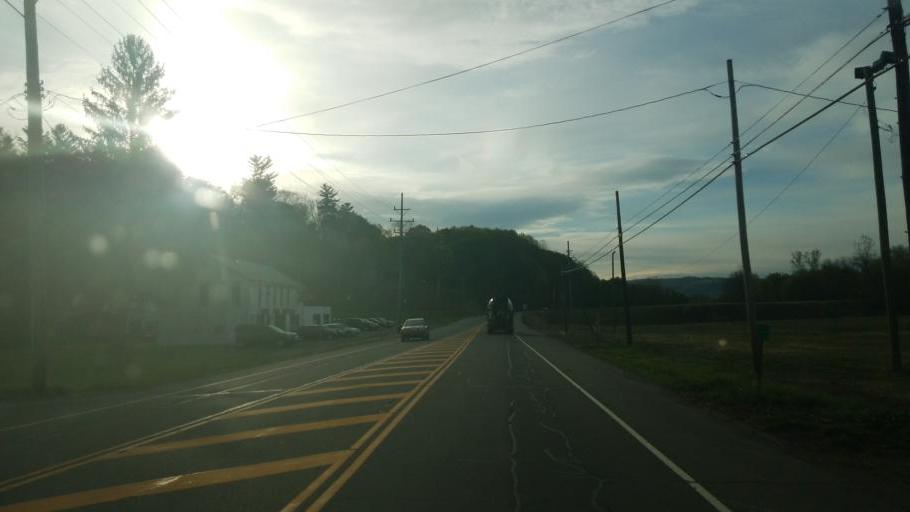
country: US
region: New York
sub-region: Steuben County
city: Hornell
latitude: 42.3339
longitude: -77.6770
